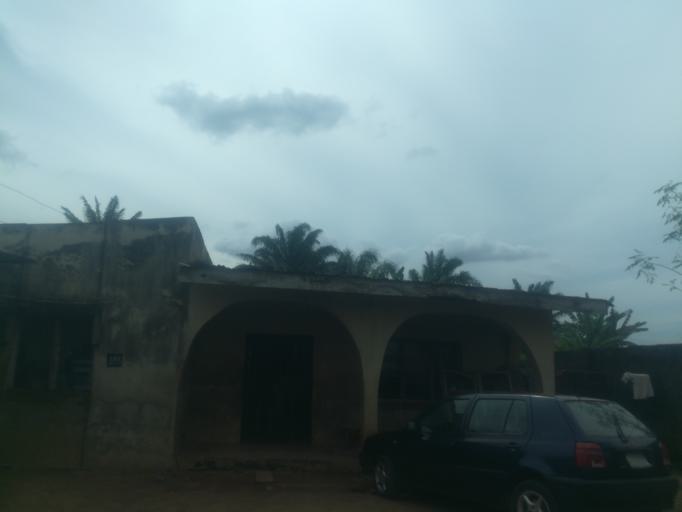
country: NG
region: Oyo
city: Ibadan
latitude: 7.3669
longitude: 3.9711
